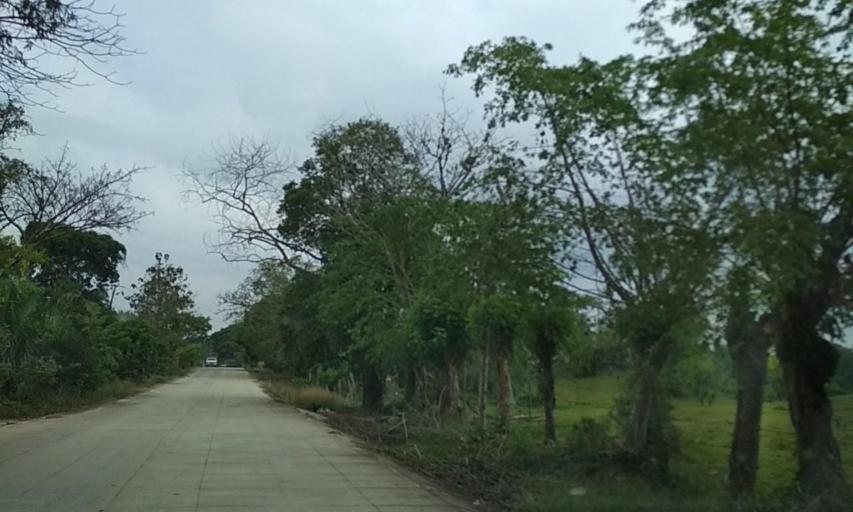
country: MX
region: Tabasco
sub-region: Huimanguillo
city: Francisco Rueda
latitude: 17.6713
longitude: -94.0910
